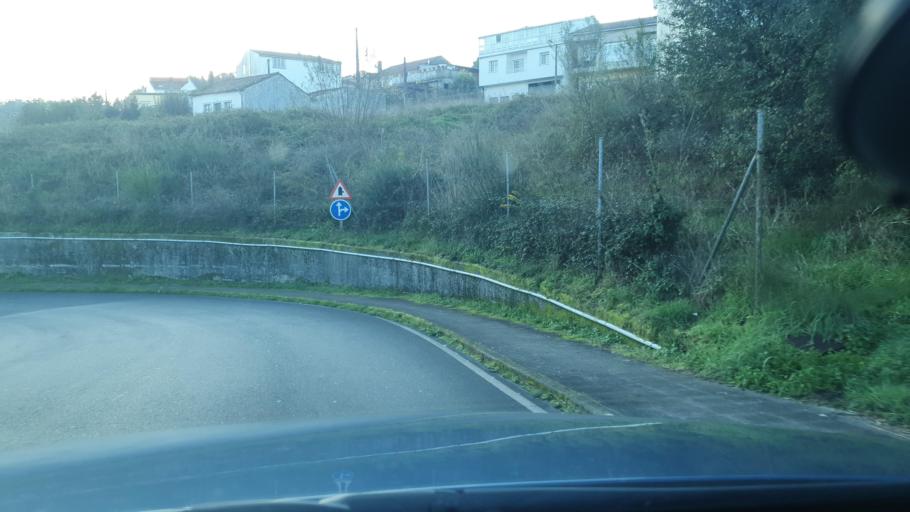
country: ES
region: Galicia
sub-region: Provincia da Coruna
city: Santiago de Compostela
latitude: 42.8591
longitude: -8.5694
